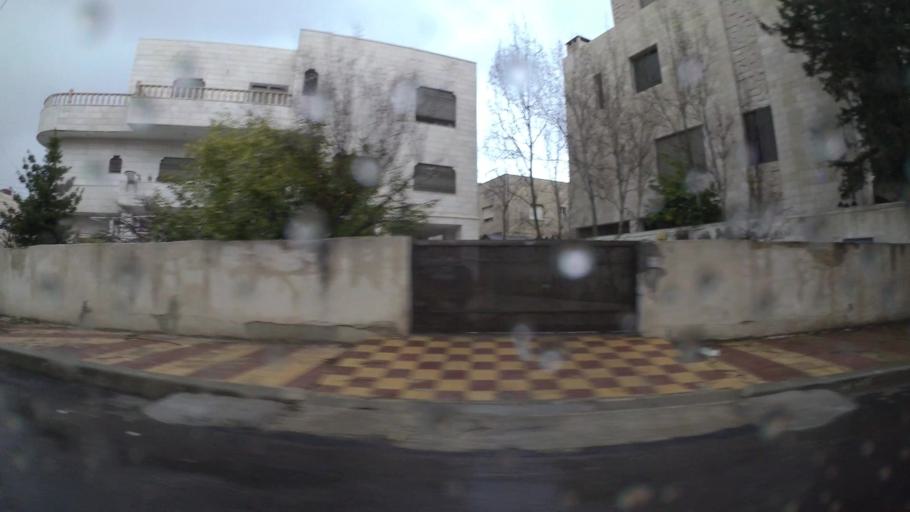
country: JO
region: Amman
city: Umm as Summaq
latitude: 31.8974
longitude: 35.8530
